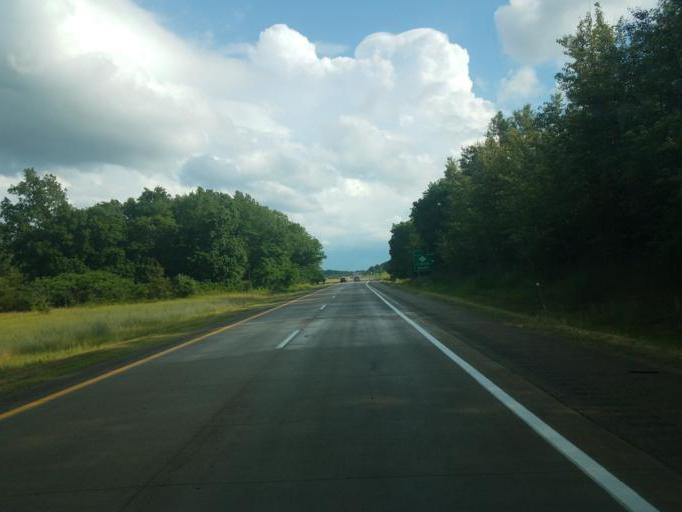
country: US
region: Michigan
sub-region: Calhoun County
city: Marshall
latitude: 42.2113
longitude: -84.9826
